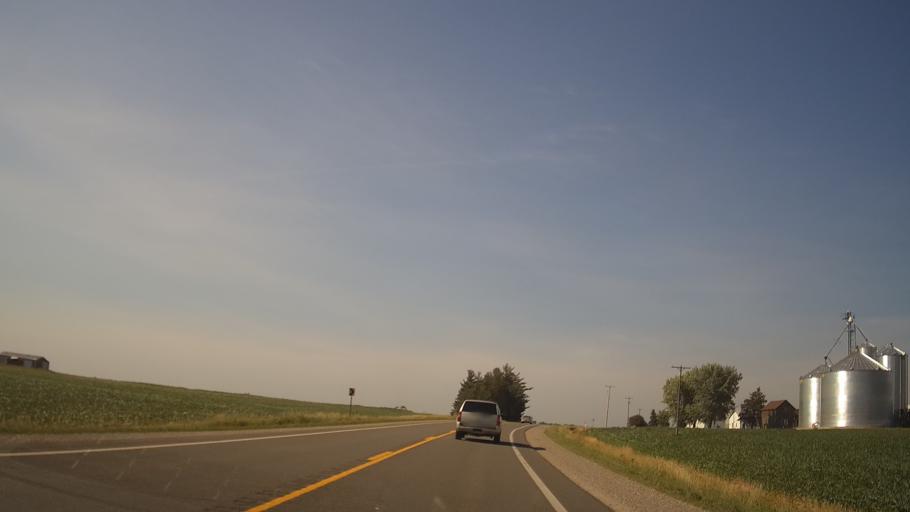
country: US
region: Michigan
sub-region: Ogemaw County
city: West Branch
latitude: 44.3566
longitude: -84.1260
